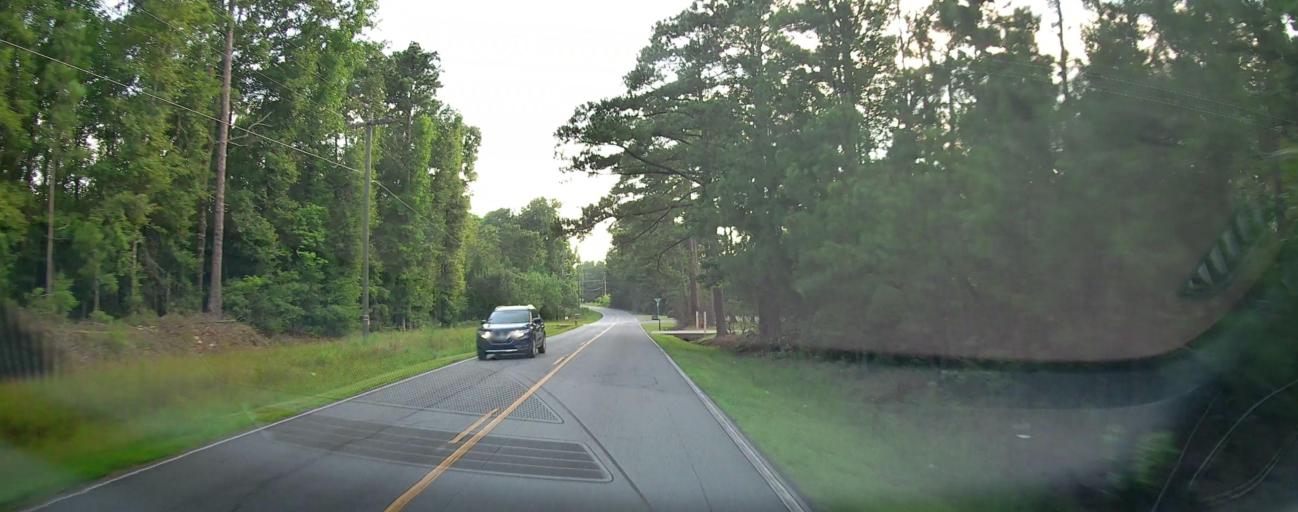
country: US
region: Georgia
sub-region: Peach County
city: Byron
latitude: 32.7231
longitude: -83.7657
